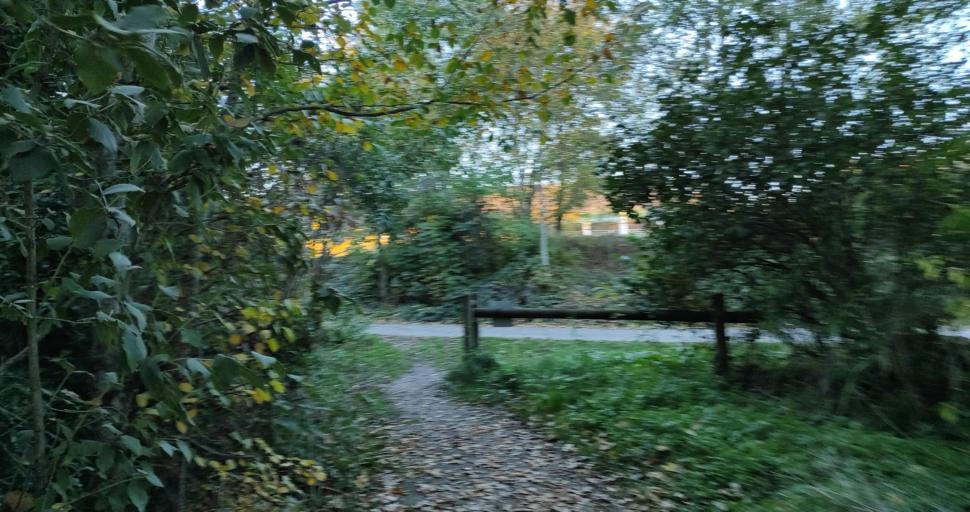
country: FR
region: Midi-Pyrenees
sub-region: Departement de l'Aveyron
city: Le Monastere
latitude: 44.3311
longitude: 2.5934
